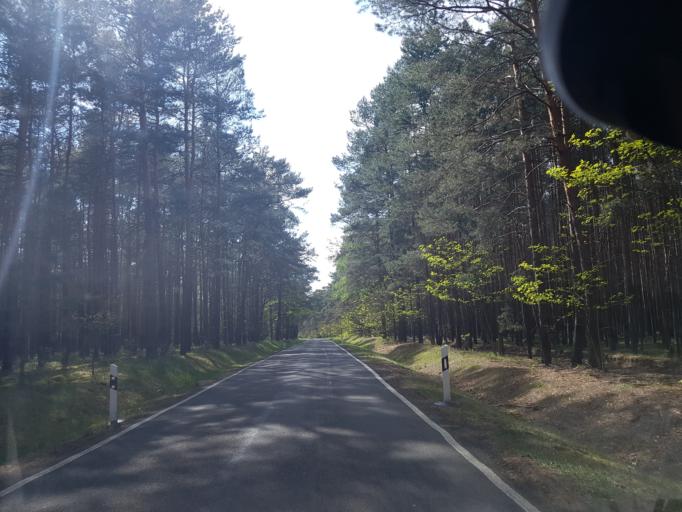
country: DE
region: Brandenburg
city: Heinersbruck
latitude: 51.6870
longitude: 14.4998
